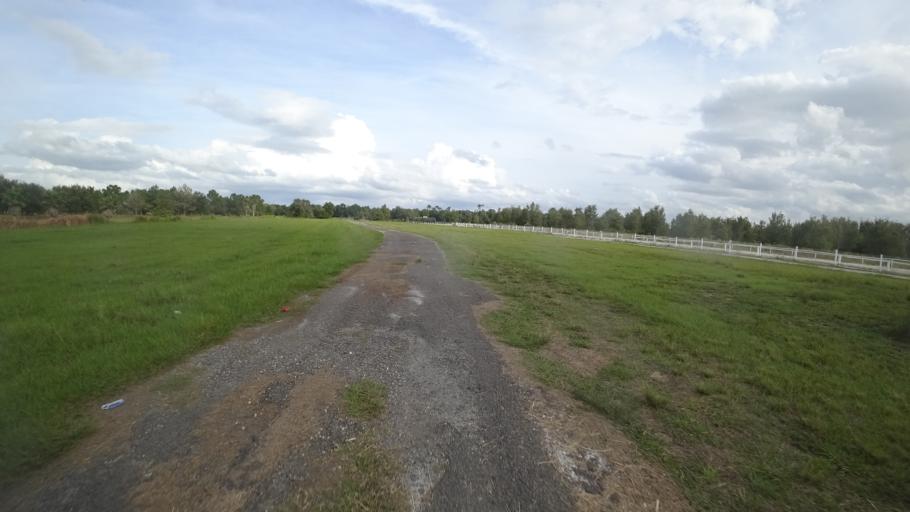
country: US
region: Florida
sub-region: Hillsborough County
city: Wimauma
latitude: 27.6048
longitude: -82.1562
